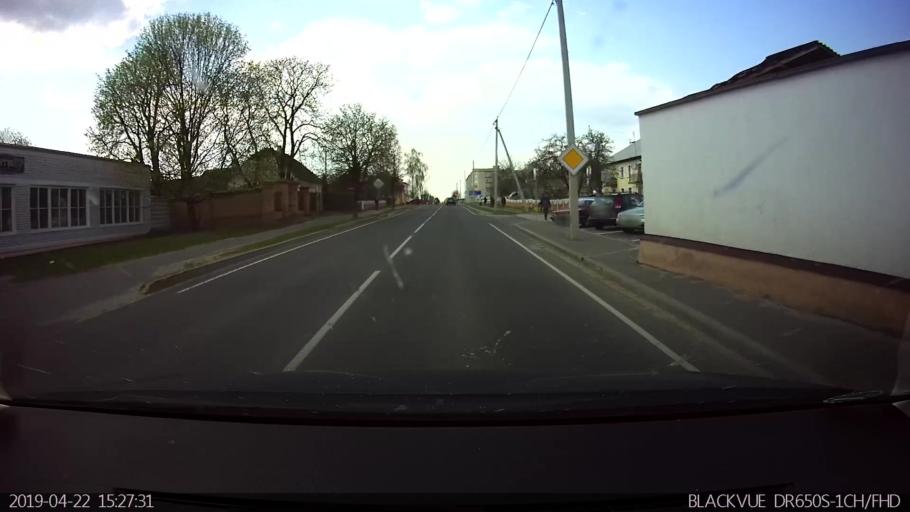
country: BY
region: Brest
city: Vysokaye
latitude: 52.3711
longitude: 23.3706
